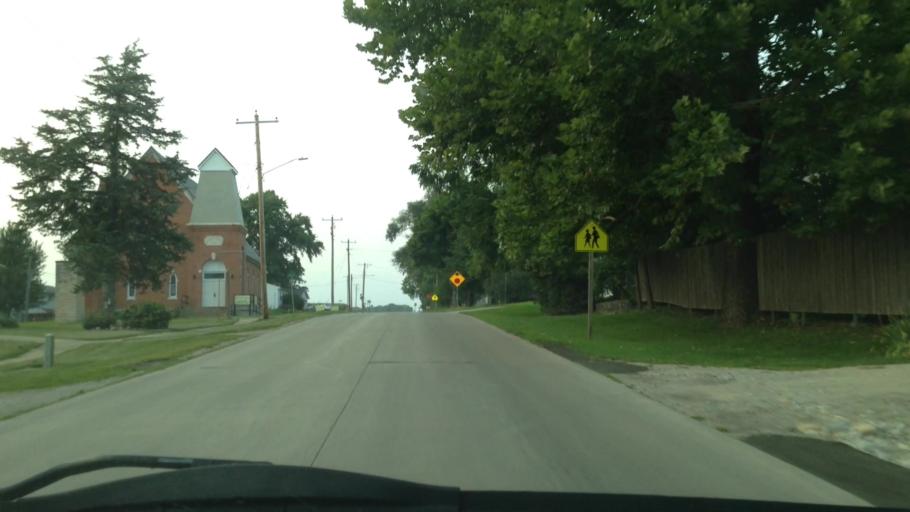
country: US
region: Iowa
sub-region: Linn County
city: Palo
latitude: 42.0949
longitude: -91.8734
